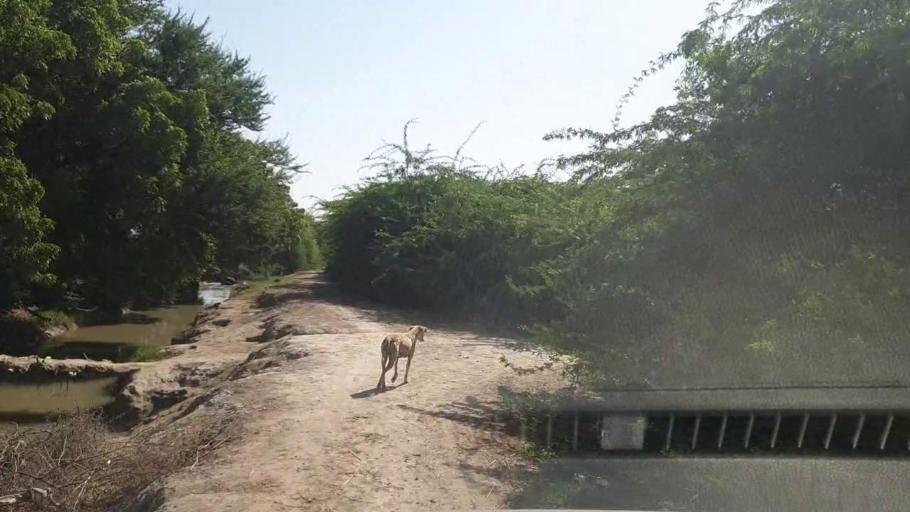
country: PK
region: Sindh
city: Kadhan
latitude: 24.6283
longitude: 68.9938
